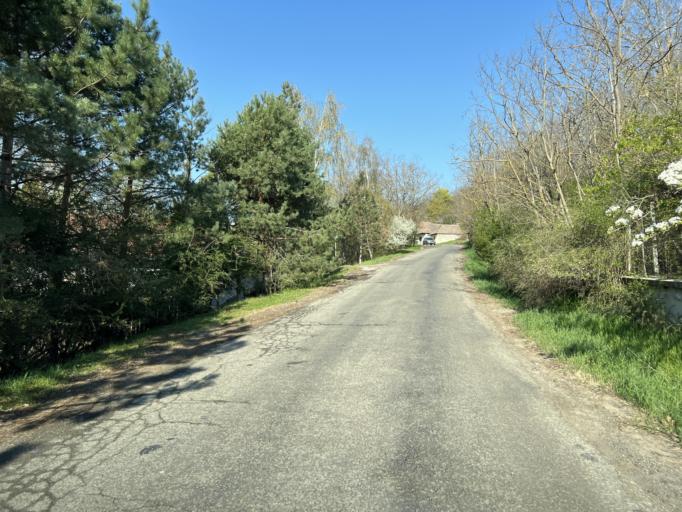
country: SK
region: Nitriansky
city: Sahy
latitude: 47.9985
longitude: 18.8586
